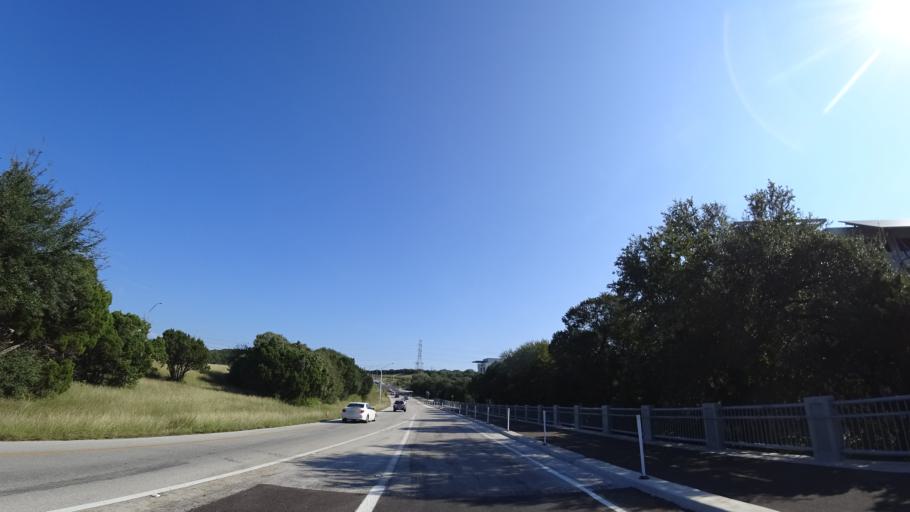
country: US
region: Texas
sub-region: Travis County
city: Rollingwood
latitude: 30.2446
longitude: -97.8068
